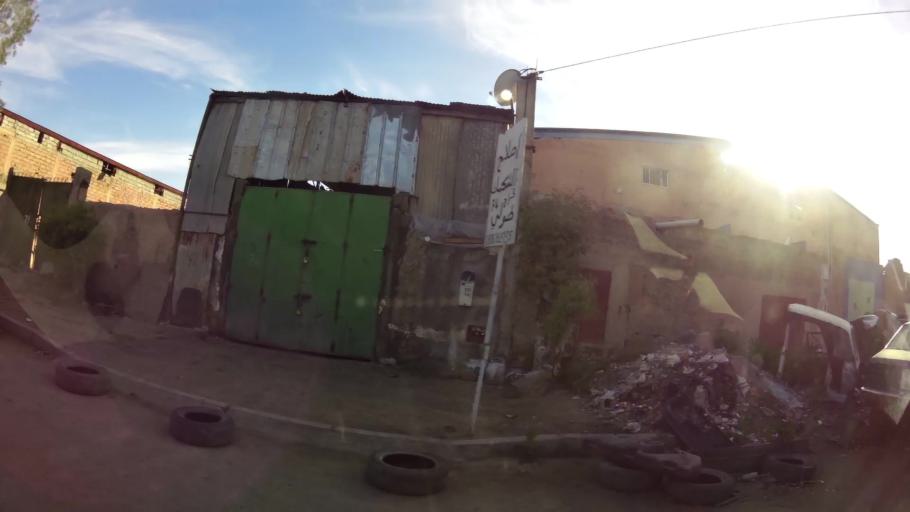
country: MA
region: Marrakech-Tensift-Al Haouz
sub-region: Marrakech
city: Marrakesh
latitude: 31.6809
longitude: -8.0534
